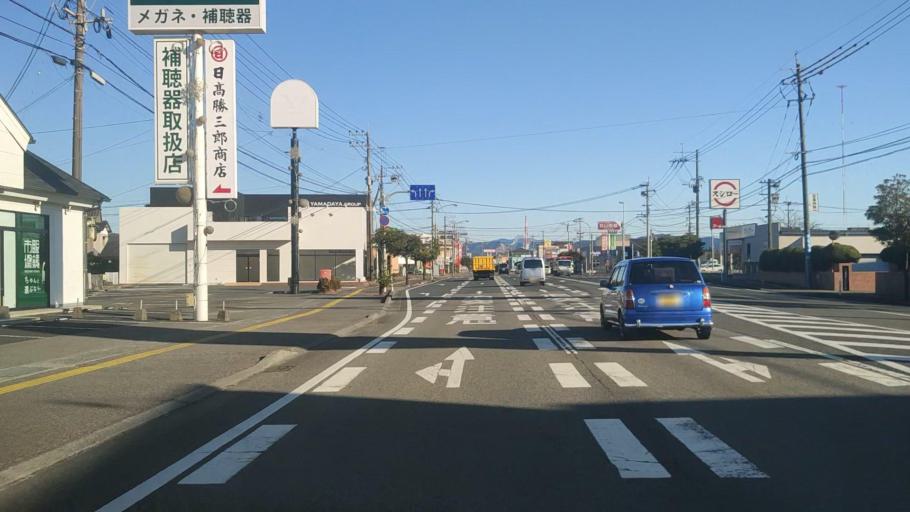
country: JP
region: Miyazaki
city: Nobeoka
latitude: 32.5507
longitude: 131.6775
